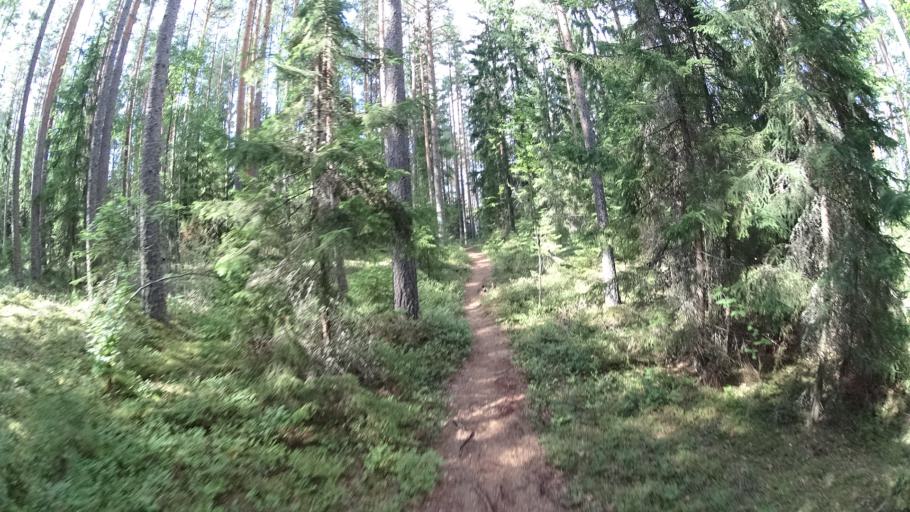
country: FI
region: Uusimaa
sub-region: Helsinki
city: Kaerkoelae
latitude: 60.7340
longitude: 24.0741
